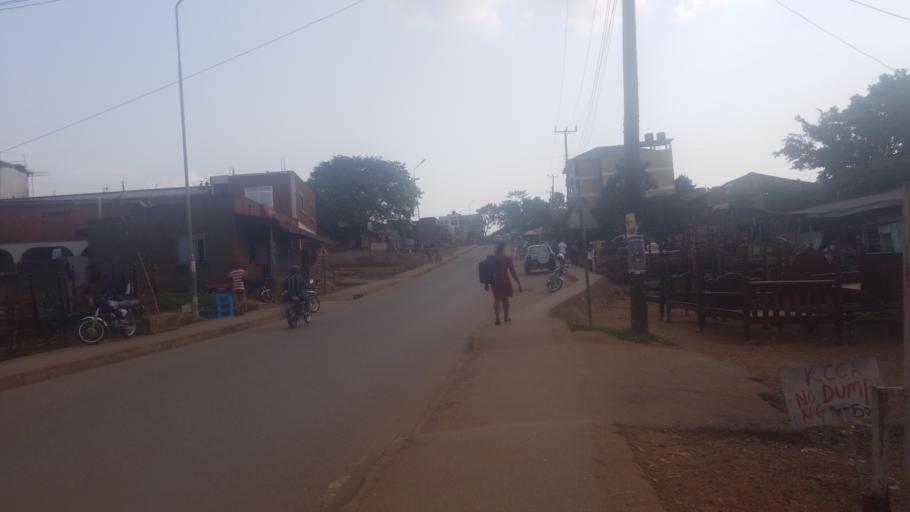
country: UG
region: Central Region
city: Kampala Central Division
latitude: 0.3339
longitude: 32.5592
